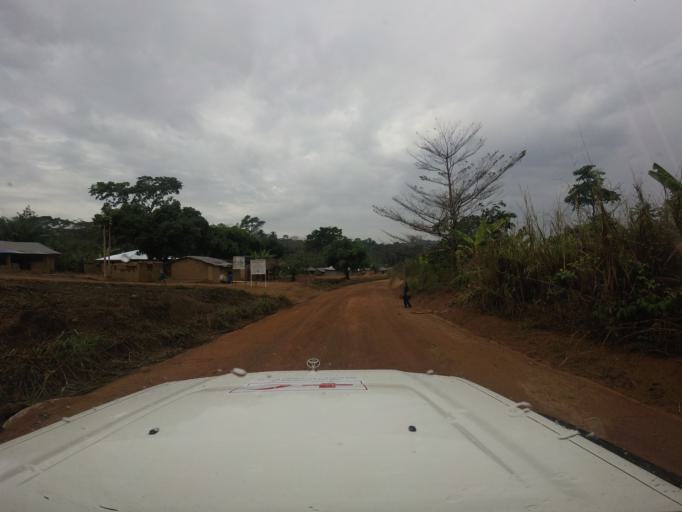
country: SL
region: Eastern Province
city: Buedu
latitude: 8.3365
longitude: -10.1693
